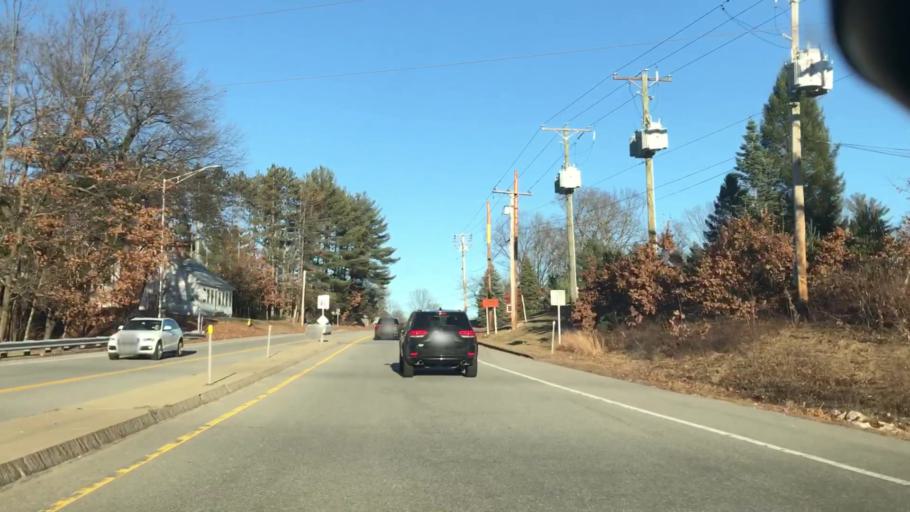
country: US
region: New Hampshire
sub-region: Hillsborough County
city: Bedford
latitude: 42.9605
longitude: -71.5006
